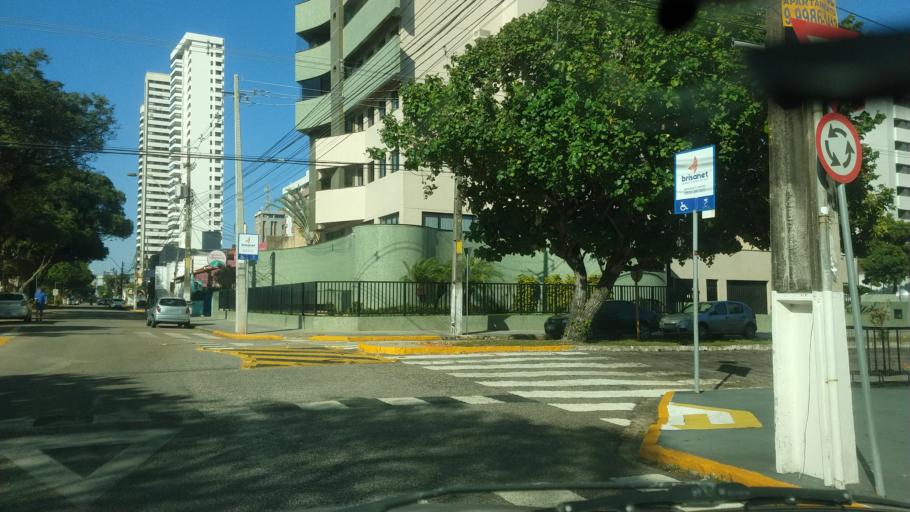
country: BR
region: Rio Grande do Norte
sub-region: Natal
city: Natal
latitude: -5.7865
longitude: -35.1994
